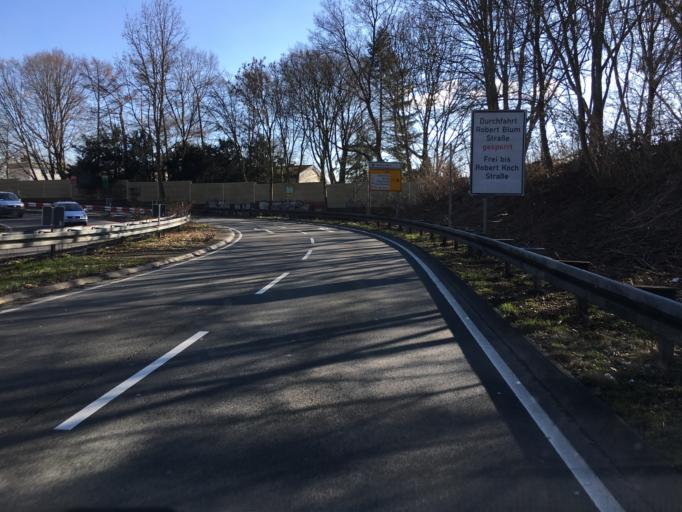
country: DE
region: North Rhine-Westphalia
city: Opladen
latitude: 51.0551
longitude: 6.9984
